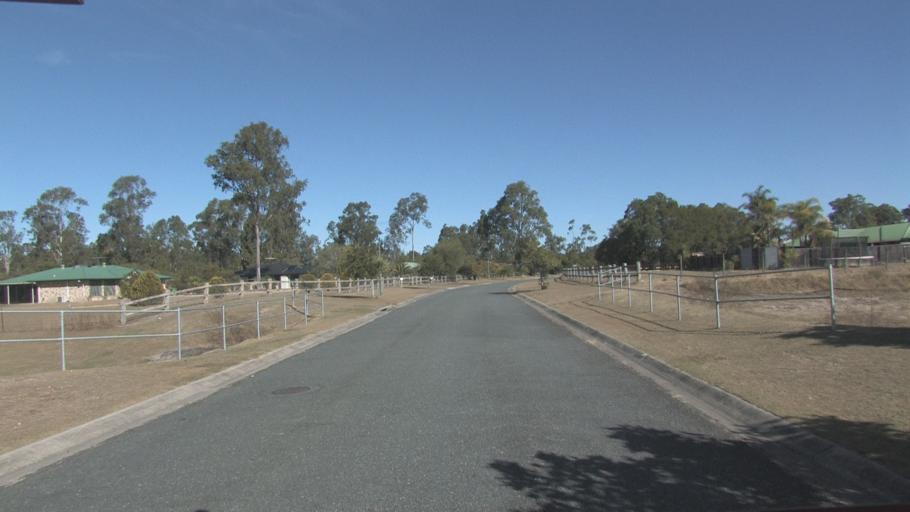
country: AU
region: Queensland
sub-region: Logan
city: North Maclean
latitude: -27.7991
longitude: 152.9694
